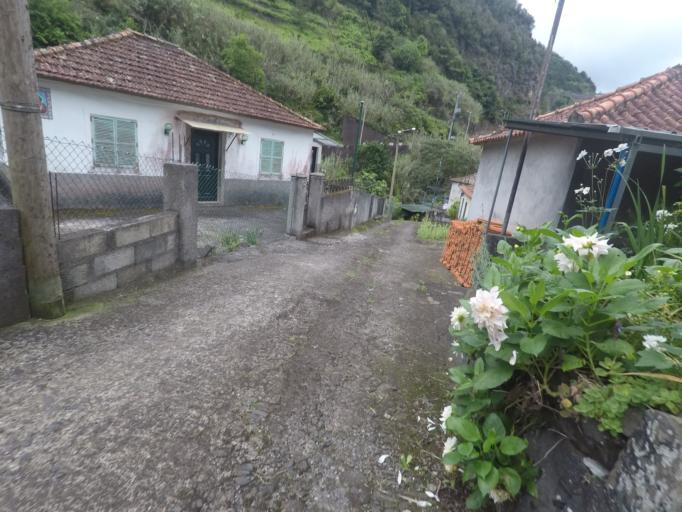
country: PT
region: Madeira
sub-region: Santana
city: Santana
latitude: 32.7636
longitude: -16.8760
